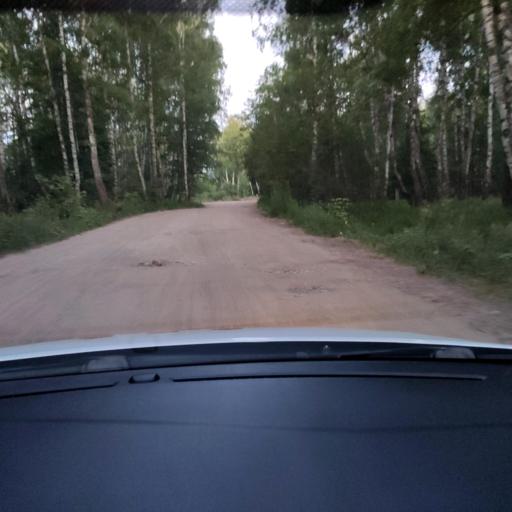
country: RU
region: Tatarstan
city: Stolbishchi
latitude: 55.7082
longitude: 49.1859
